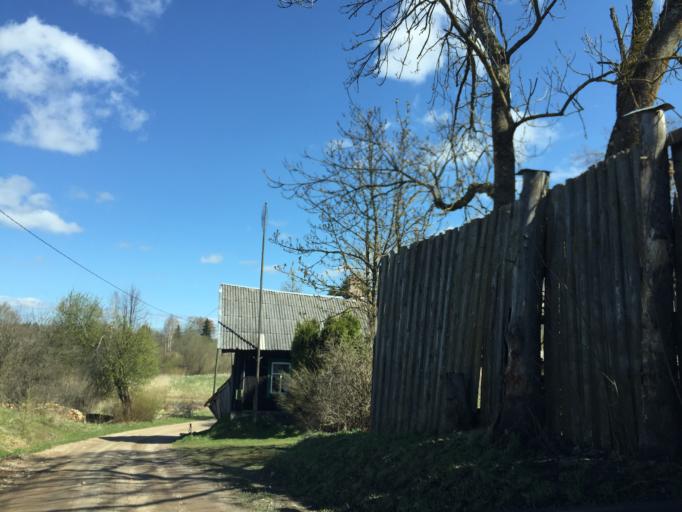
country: LV
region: Rezekne
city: Rezekne
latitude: 56.6070
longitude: 27.2140
